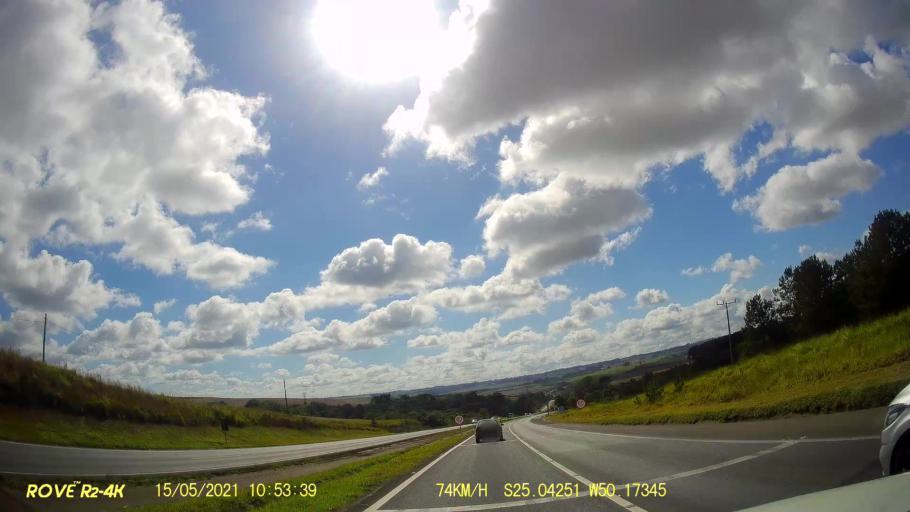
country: BR
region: Parana
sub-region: Ponta Grossa
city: Ponta Grossa
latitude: -25.0427
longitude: -50.1740
